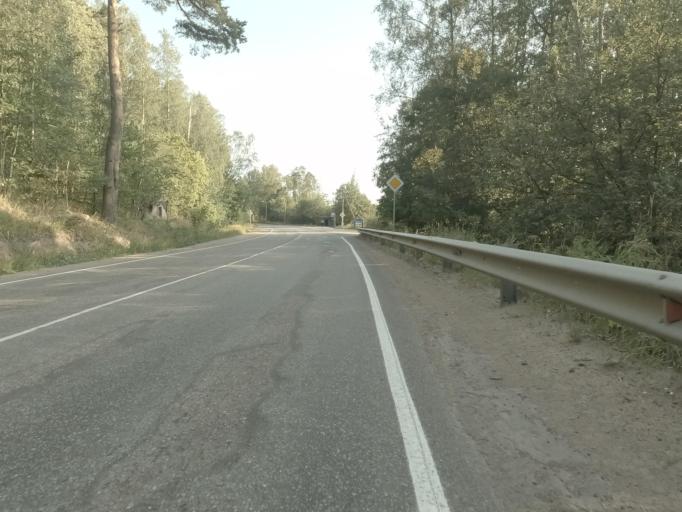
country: RU
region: Leningrad
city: Vyborg
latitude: 60.7371
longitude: 28.7581
